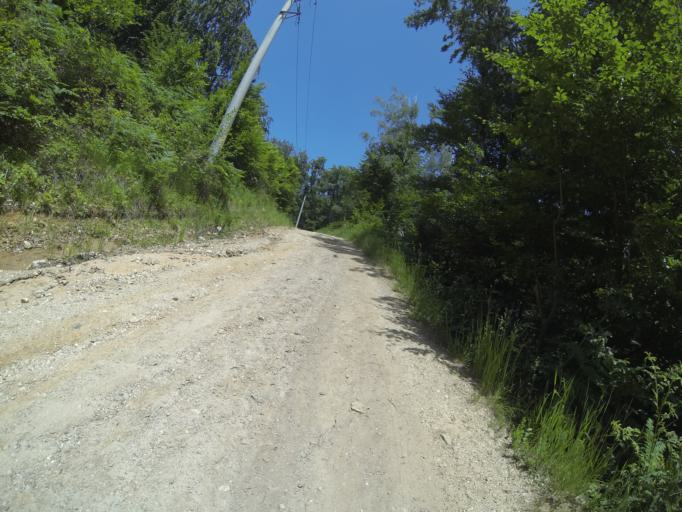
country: RO
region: Valcea
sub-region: Oras Baile Olanesti
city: Cheia
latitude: 45.2086
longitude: 24.2060
